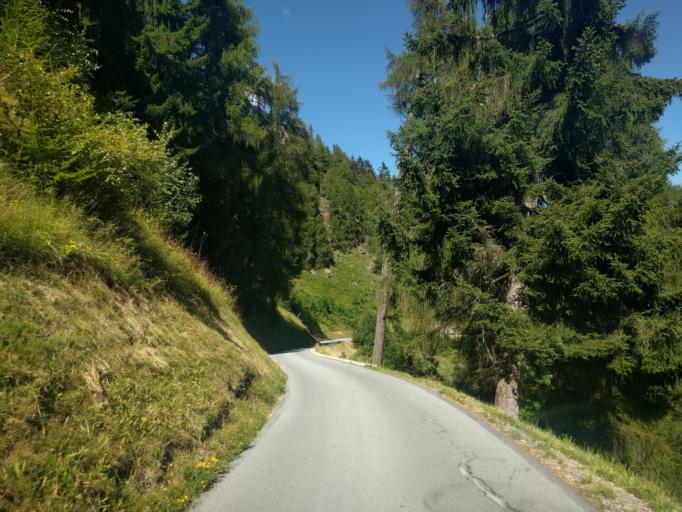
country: IT
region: Trentino-Alto Adige
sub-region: Bolzano
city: Tubre
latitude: 46.6094
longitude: 10.4169
